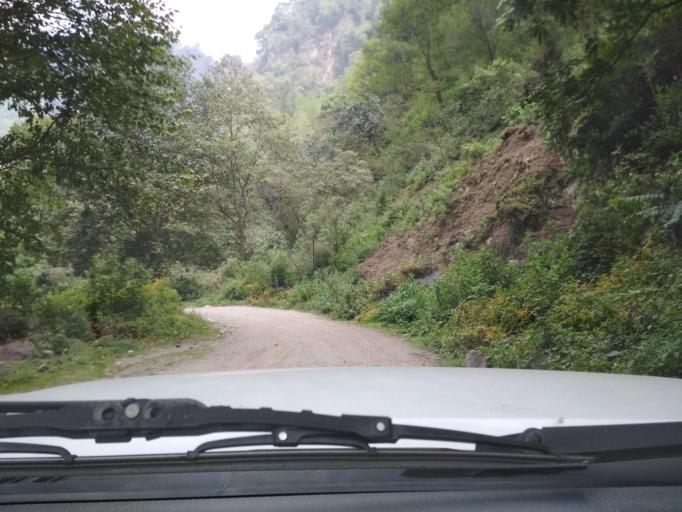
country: MX
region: Veracruz
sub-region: La Perla
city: Metlac Hernandez (Metlac Primero)
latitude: 18.9908
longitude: -97.1194
